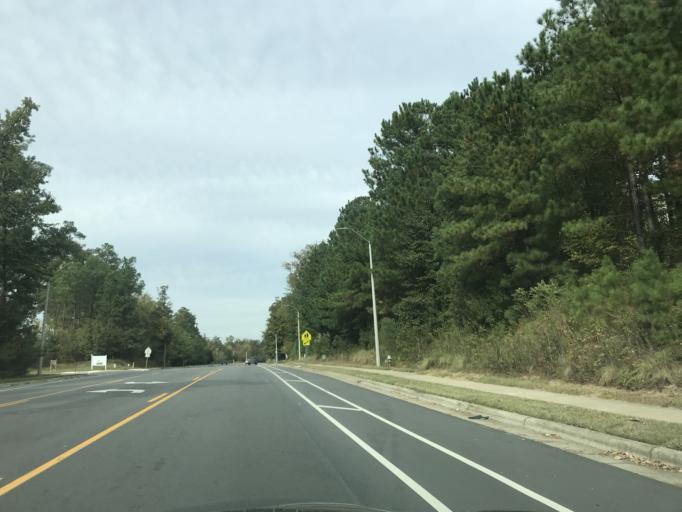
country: US
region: North Carolina
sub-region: Wake County
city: Wake Forest
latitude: 35.9506
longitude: -78.5456
